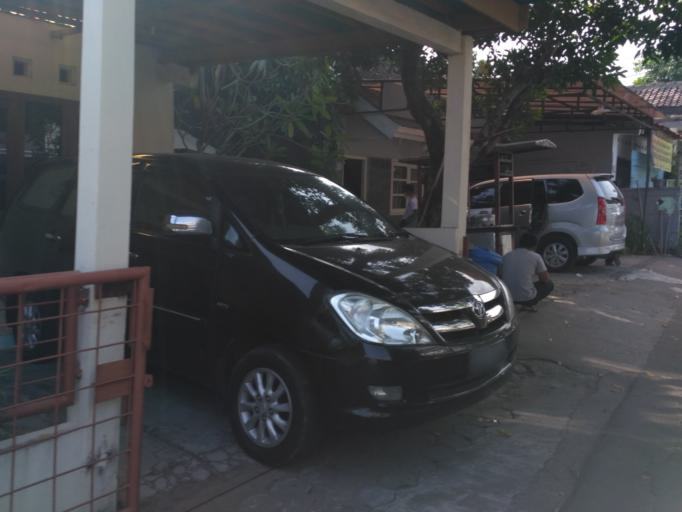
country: ID
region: Daerah Istimewa Yogyakarta
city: Depok
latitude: -7.7825
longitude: 110.4318
